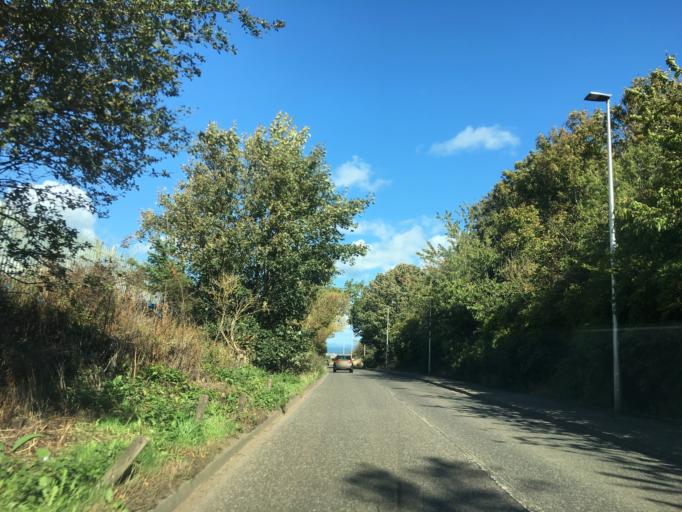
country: GB
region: Scotland
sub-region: Midlothian
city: Bonnyrigg
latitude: 55.9205
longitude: -3.1143
